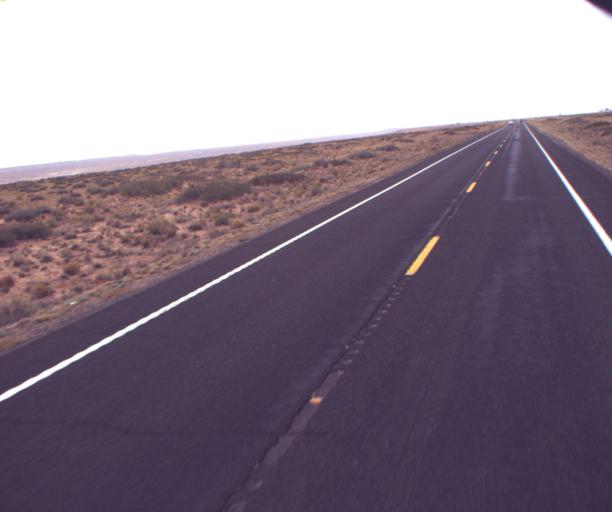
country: US
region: Arizona
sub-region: Coconino County
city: Tuba City
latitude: 36.1578
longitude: -111.1141
